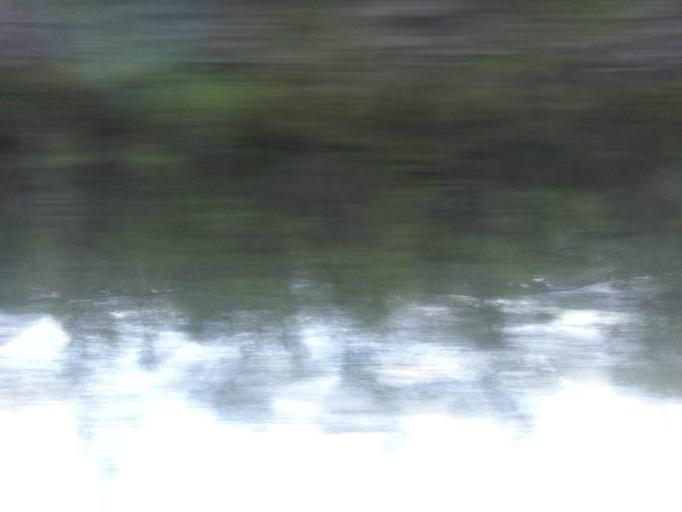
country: NO
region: Oppland
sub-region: Dovre
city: Dovre
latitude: 62.2013
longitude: 9.5264
